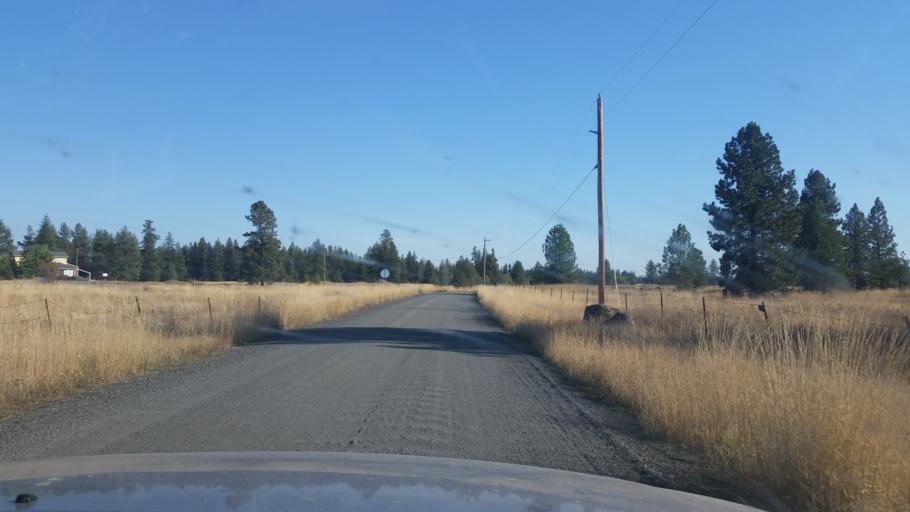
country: US
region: Washington
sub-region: Spokane County
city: Cheney
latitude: 47.4340
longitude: -117.6606
